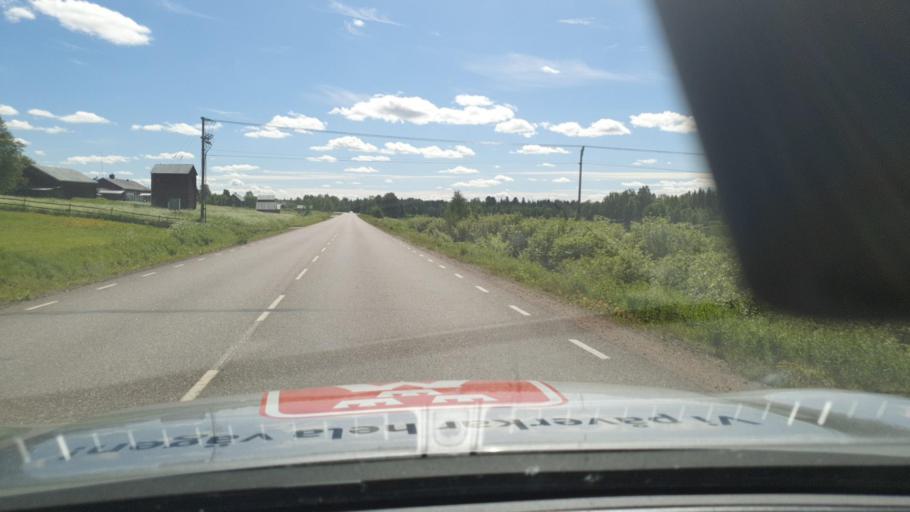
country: SE
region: Norrbotten
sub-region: Pajala Kommun
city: Pajala
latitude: 67.1662
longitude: 22.6163
